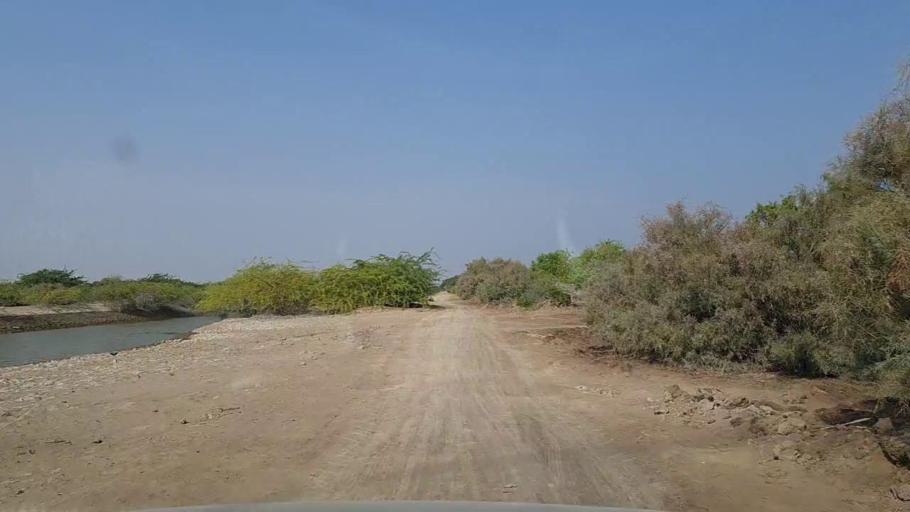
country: PK
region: Sindh
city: Mirpur Sakro
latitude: 24.5501
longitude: 67.5566
